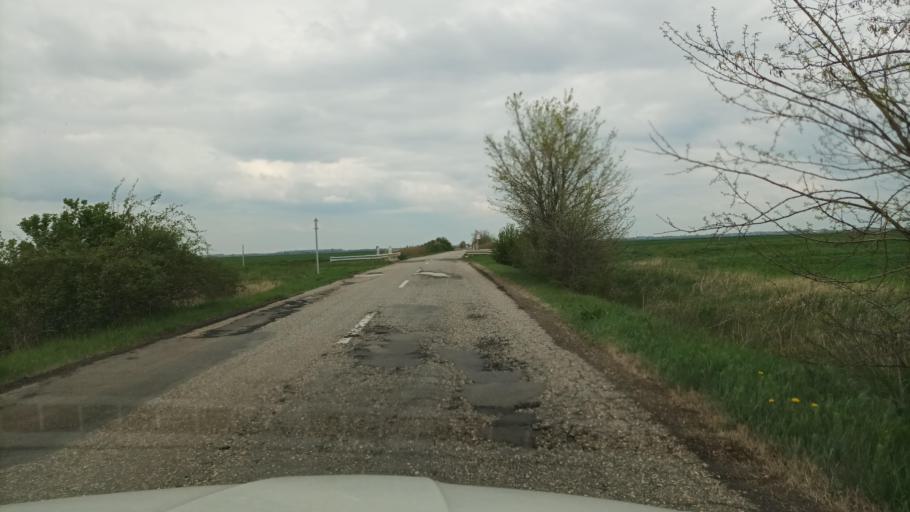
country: HU
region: Pest
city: Tortel
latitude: 47.1445
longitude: 19.9587
